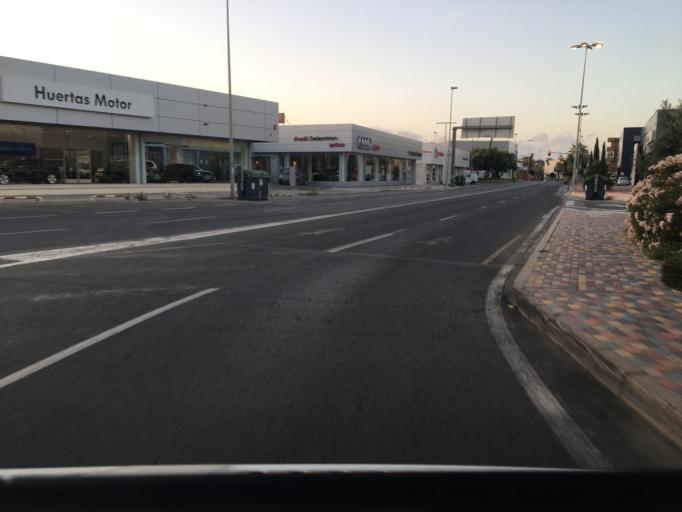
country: ES
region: Murcia
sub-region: Murcia
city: Cartagena
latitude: 37.6285
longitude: -1.0024
